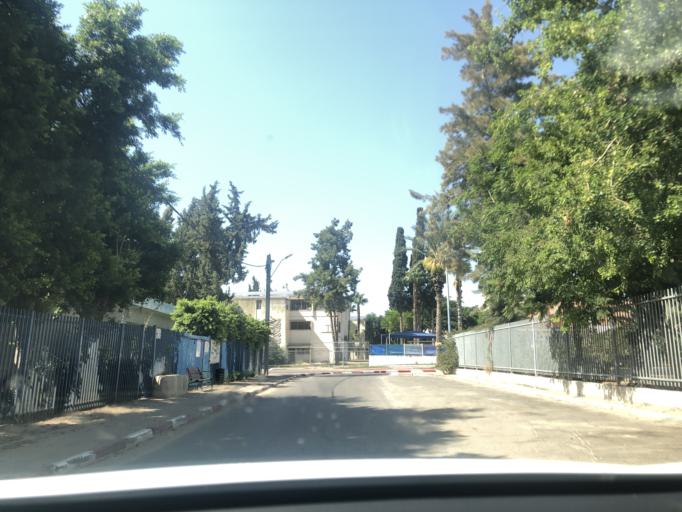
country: IL
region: Central District
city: Lod
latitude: 31.9518
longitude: 34.8928
